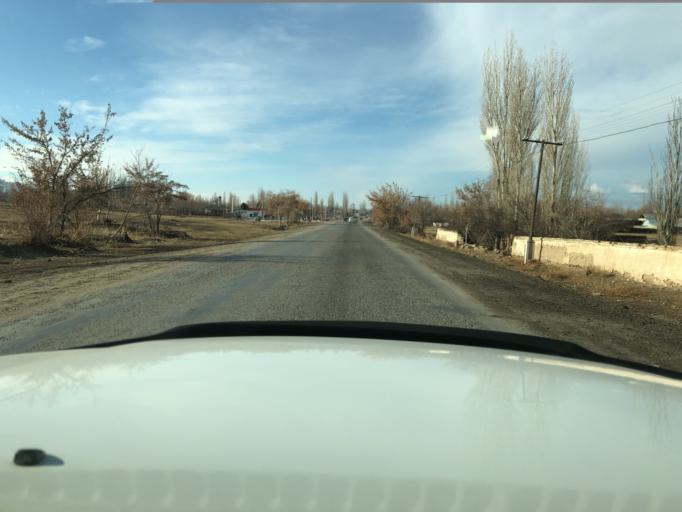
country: KG
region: Ysyk-Koel
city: Pokrovka
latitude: 42.3256
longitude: 77.9434
